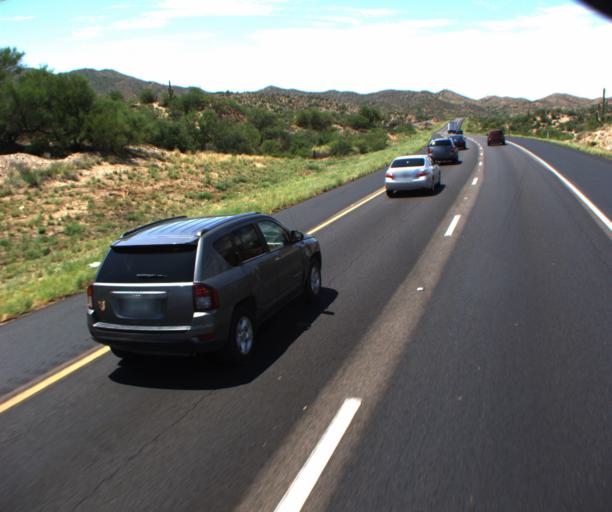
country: US
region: Arizona
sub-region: Pinal County
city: Gold Camp
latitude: 33.2751
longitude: -111.2029
